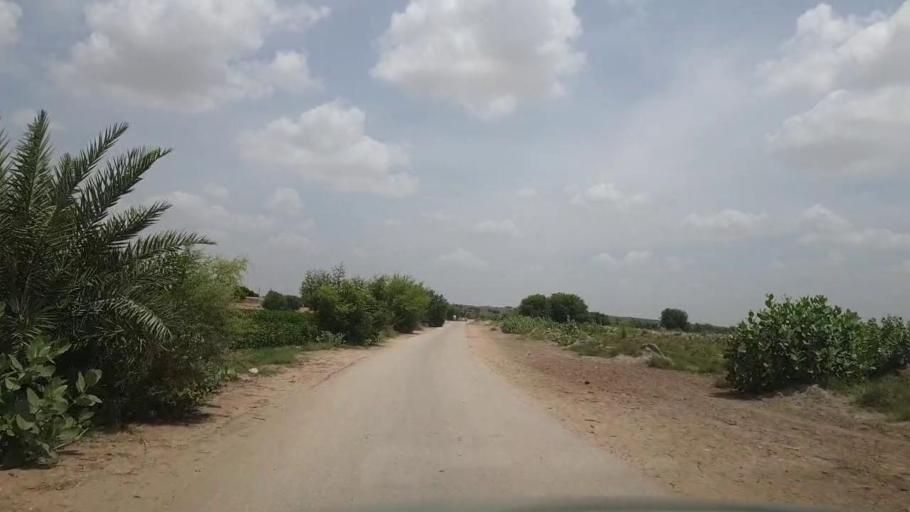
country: PK
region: Sindh
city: Kot Diji
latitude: 27.2009
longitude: 69.0602
